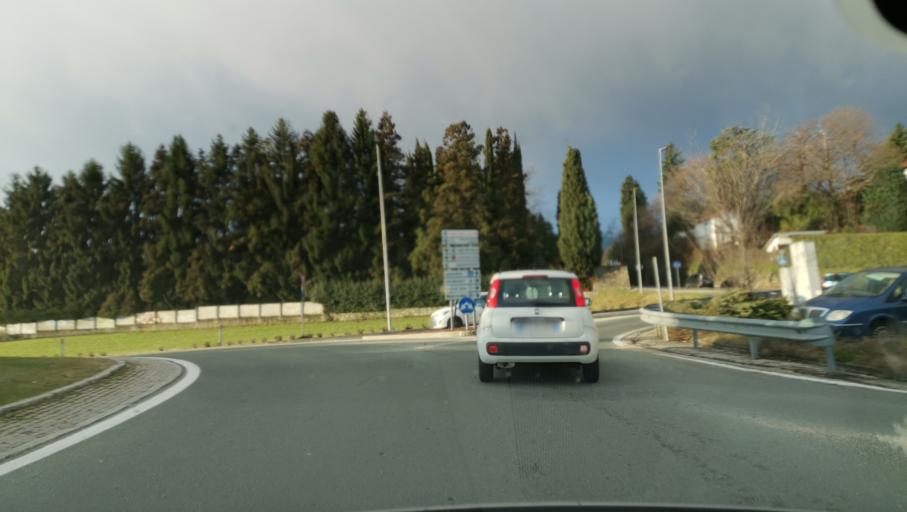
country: IT
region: Piedmont
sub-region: Provincia di Torino
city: Giaveno
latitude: 45.0481
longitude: 7.3581
